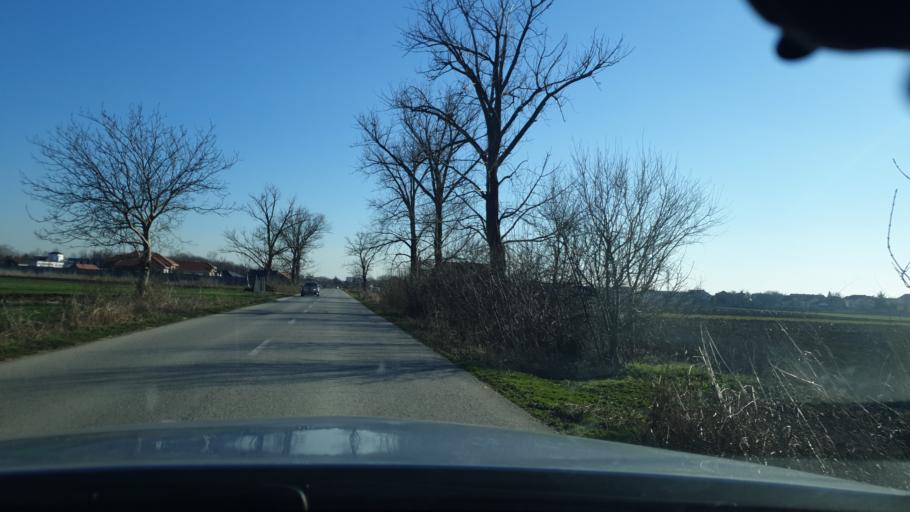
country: RS
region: Autonomna Pokrajina Vojvodina
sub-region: Sremski Okrug
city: Ruma
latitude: 45.0231
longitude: 19.8140
